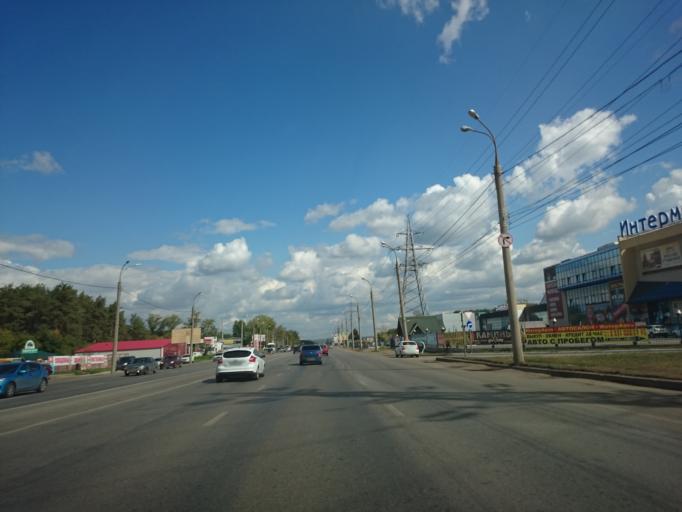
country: RU
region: Samara
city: Samara
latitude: 53.2622
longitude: 50.2414
